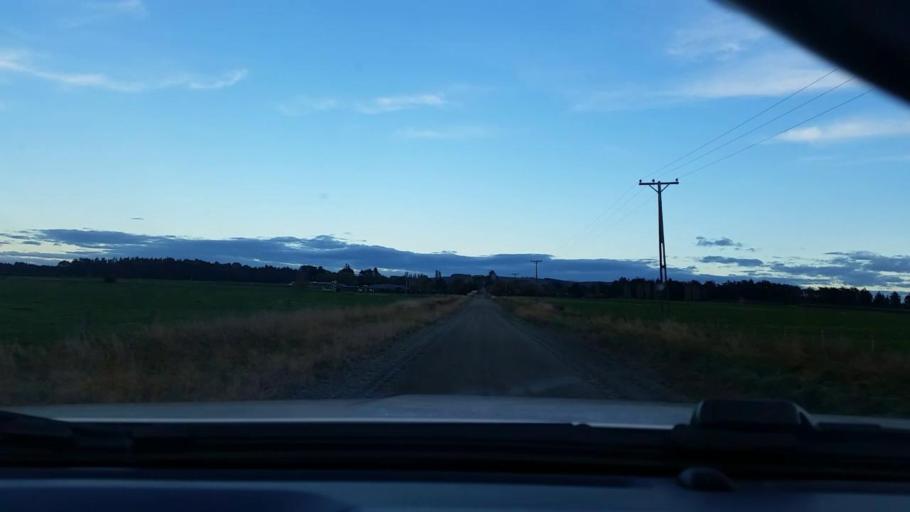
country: NZ
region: Southland
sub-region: Southland District
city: Winton
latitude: -46.1013
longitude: 168.4702
